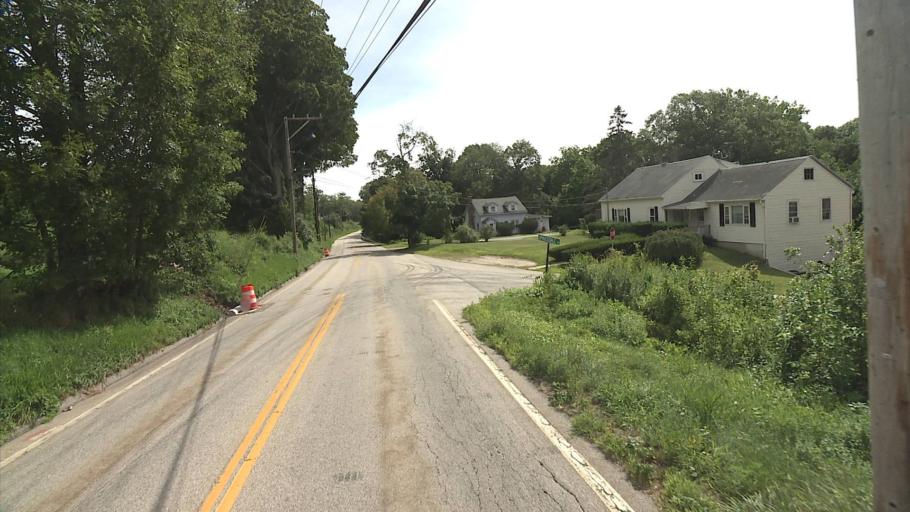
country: US
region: Connecticut
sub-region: Windham County
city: South Woodstock
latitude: 41.9372
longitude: -71.9783
